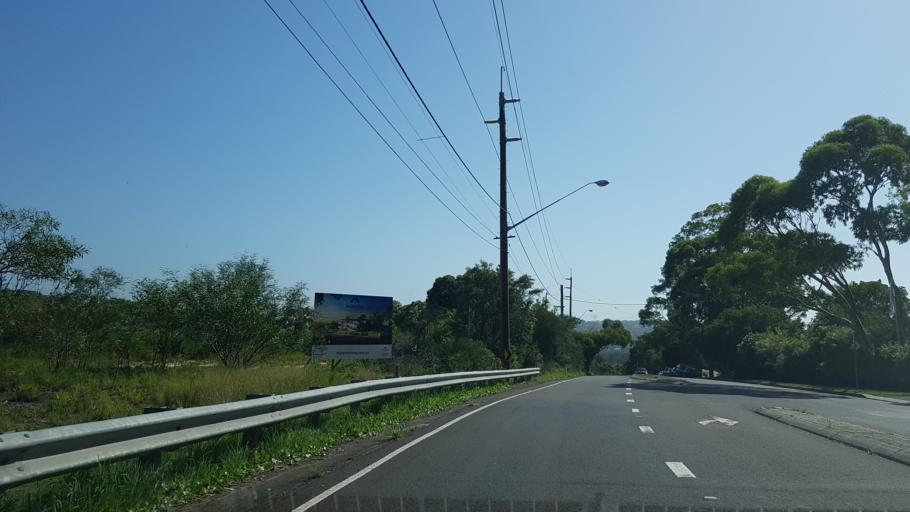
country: AU
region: New South Wales
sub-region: Warringah
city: Narraweena
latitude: -33.7445
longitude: 151.2652
